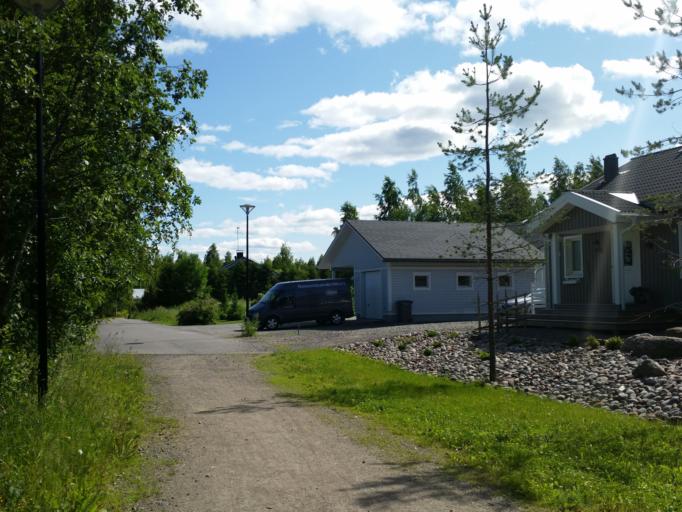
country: FI
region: Northern Savo
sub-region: Varkaus
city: Varkaus
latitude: 62.3370
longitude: 27.9032
